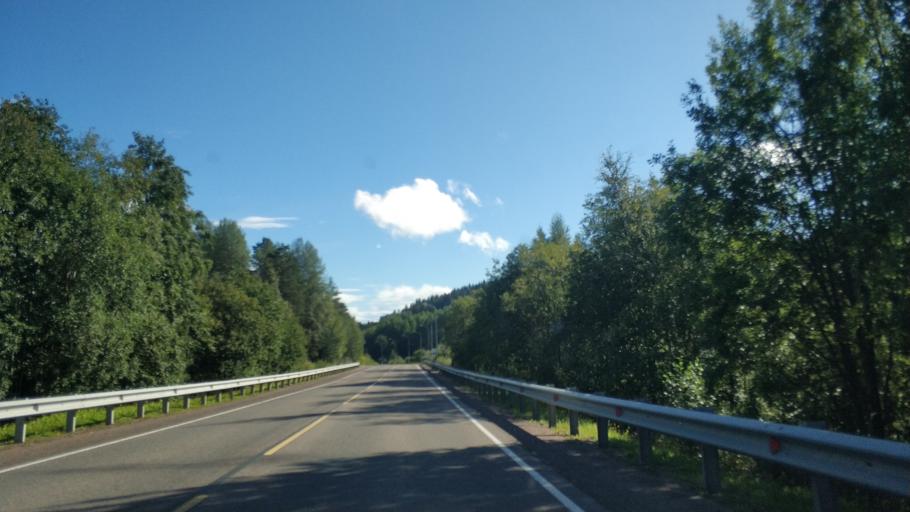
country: RU
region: Republic of Karelia
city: Sortavala
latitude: 61.6691
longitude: 30.6540
